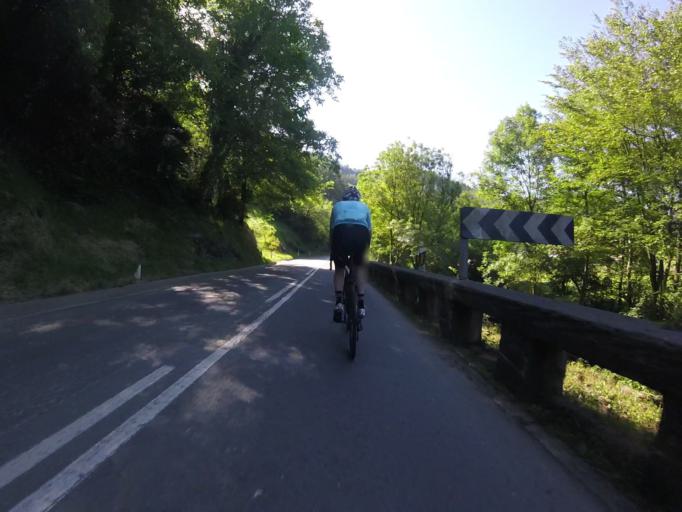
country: ES
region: Basque Country
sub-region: Provincia de Guipuzcoa
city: Beizama
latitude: 43.1473
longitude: -2.2335
